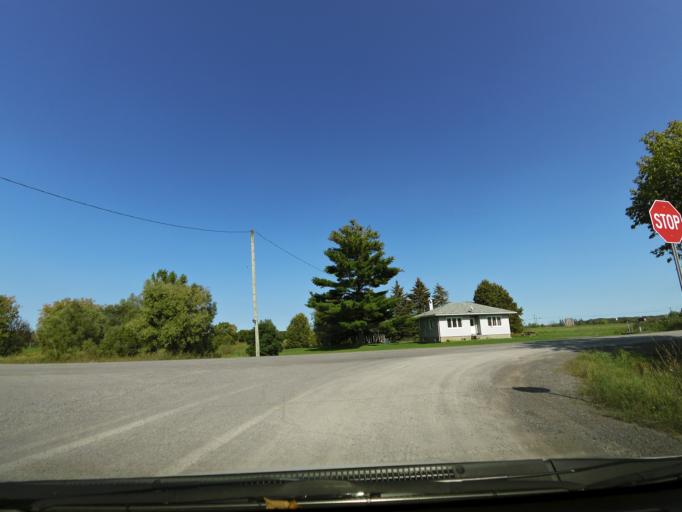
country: CA
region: Ontario
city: Carleton Place
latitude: 45.3188
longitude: -76.0508
